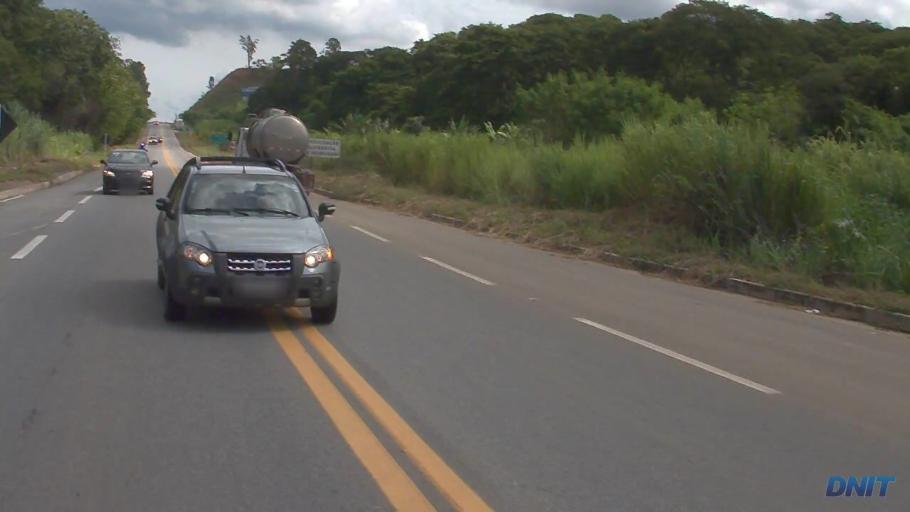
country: BR
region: Minas Gerais
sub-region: Ipatinga
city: Ipatinga
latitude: -19.4418
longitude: -42.5122
